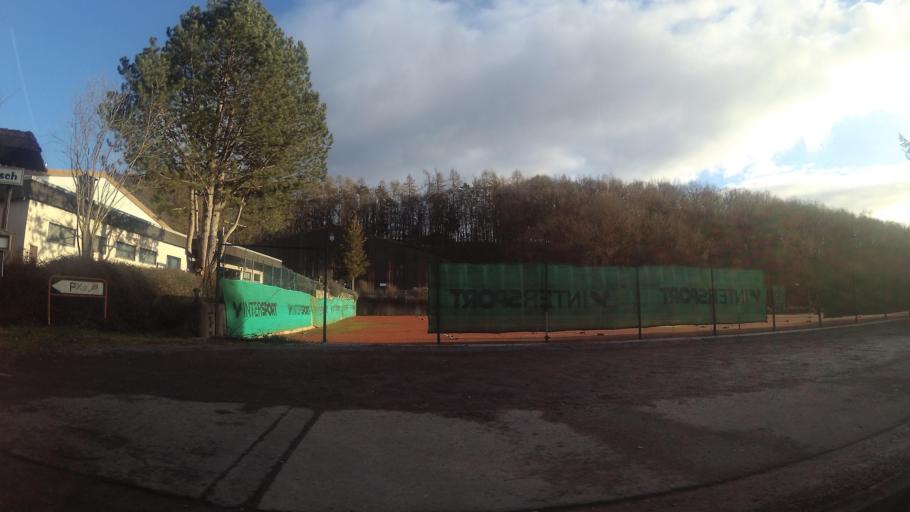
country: DE
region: Rheinland-Pfalz
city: Kusel
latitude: 49.5477
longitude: 7.3931
